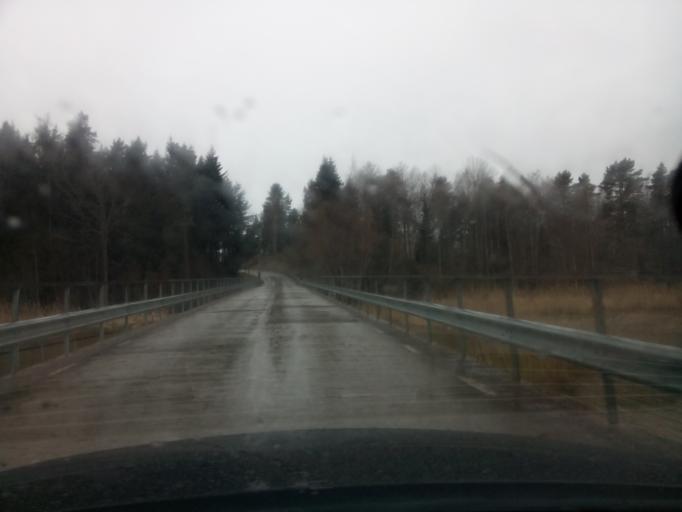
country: SE
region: Soedermanland
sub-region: Nykopings Kommun
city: Olstorp
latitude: 58.8649
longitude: 16.7091
